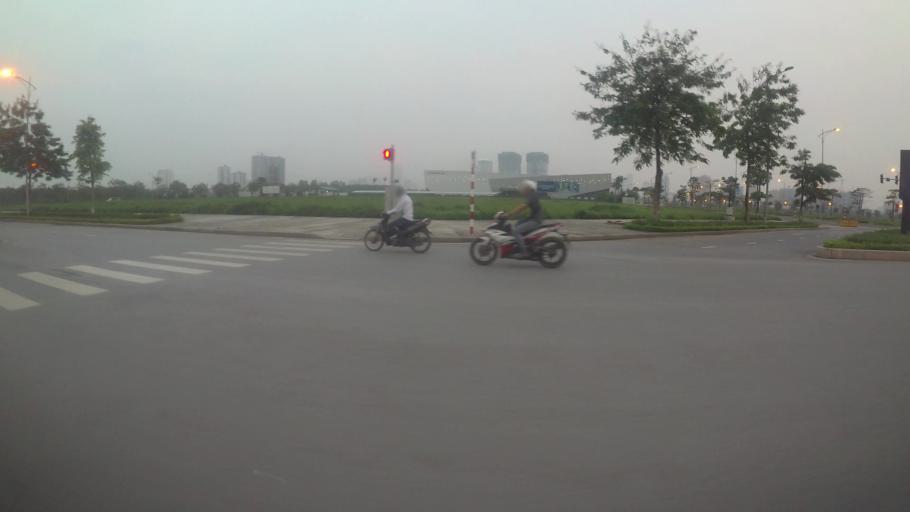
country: VN
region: Ha Noi
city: Tay Ho
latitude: 21.0624
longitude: 105.7982
